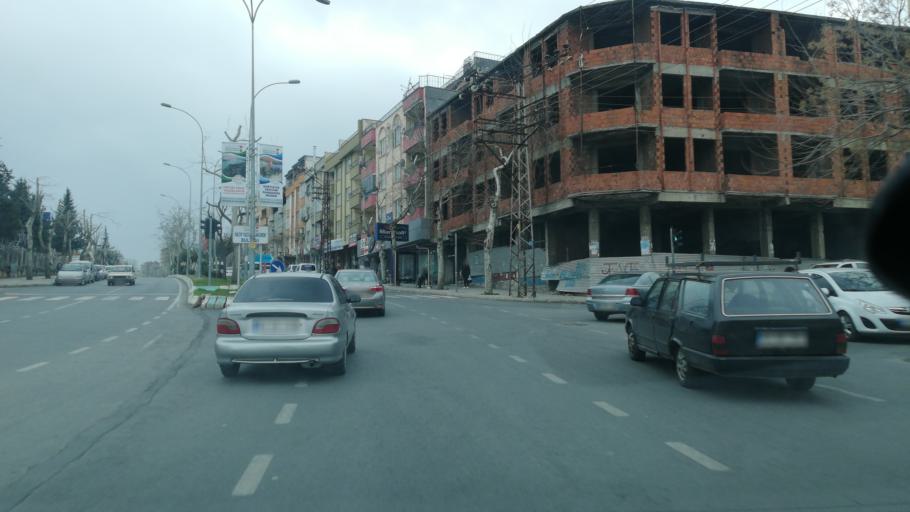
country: TR
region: Kahramanmaras
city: Kahramanmaras
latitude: 37.5889
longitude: 36.9122
